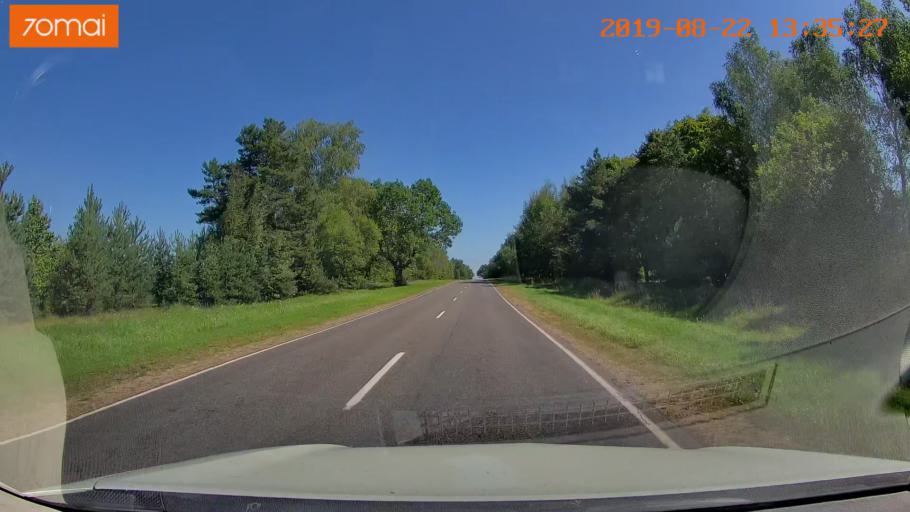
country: BY
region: Minsk
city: Staryya Darohi
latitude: 53.2136
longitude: 28.2685
